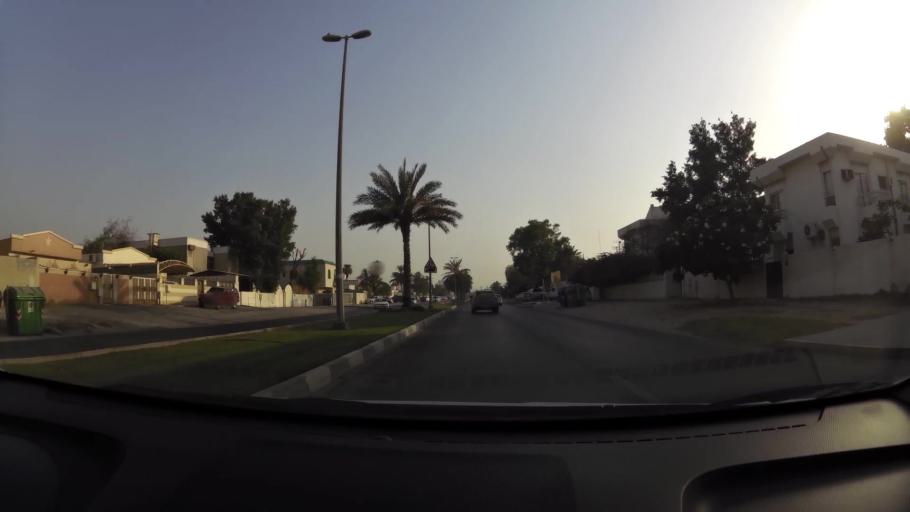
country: AE
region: Ash Shariqah
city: Sharjah
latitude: 25.3674
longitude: 55.4225
